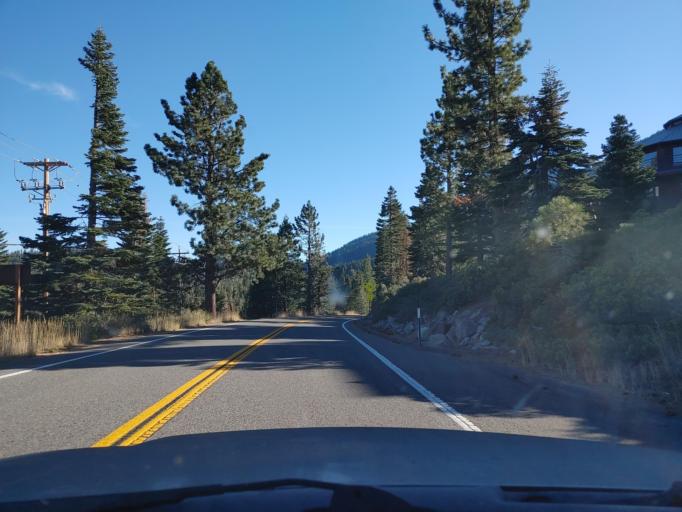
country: US
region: California
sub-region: Placer County
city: Tahoma
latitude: 39.0101
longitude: -120.1165
